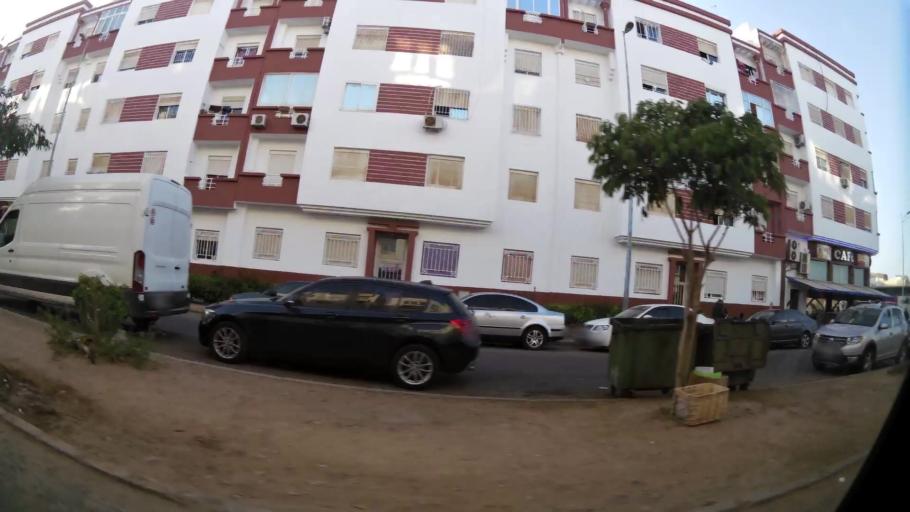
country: MA
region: Oued ed Dahab-Lagouira
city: Dakhla
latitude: 30.3987
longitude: -9.5513
